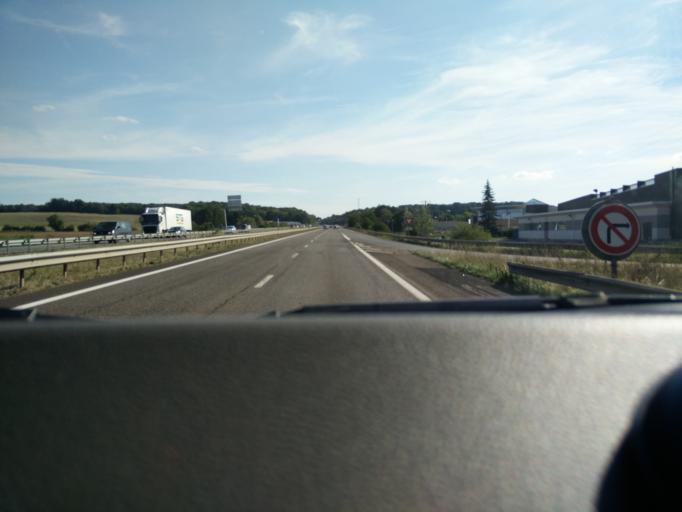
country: FR
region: Lorraine
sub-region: Departement de Meurthe-et-Moselle
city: Pont-a-Mousson
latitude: 48.9345
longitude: 6.1118
